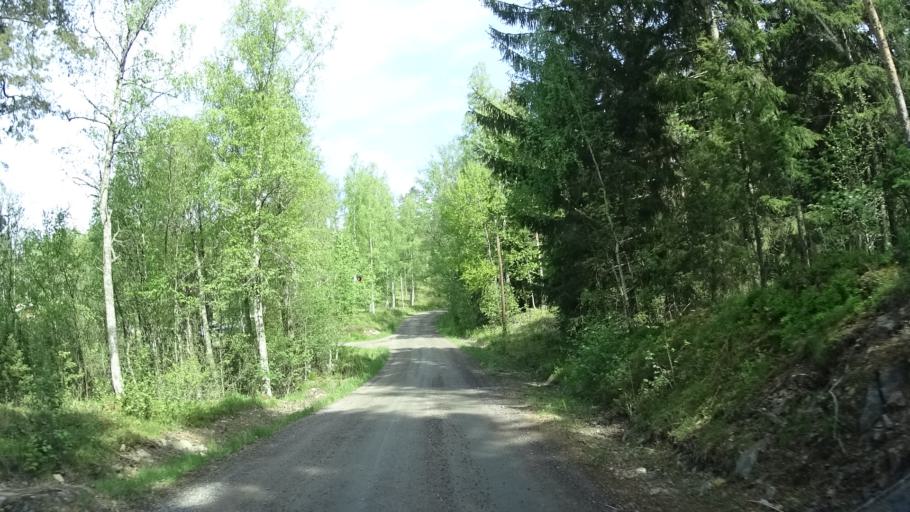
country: SE
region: OEstergoetland
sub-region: Finspangs Kommun
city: Finspang
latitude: 58.7573
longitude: 15.8356
